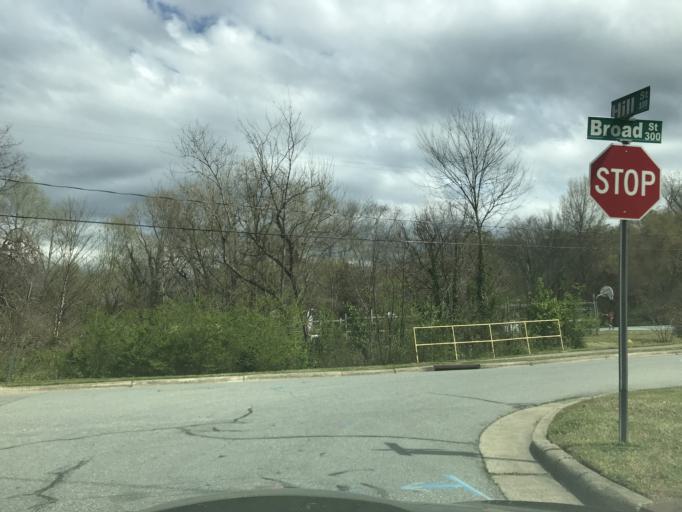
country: US
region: North Carolina
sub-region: Orange County
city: Carrboro
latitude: 35.9152
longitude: -79.0687
